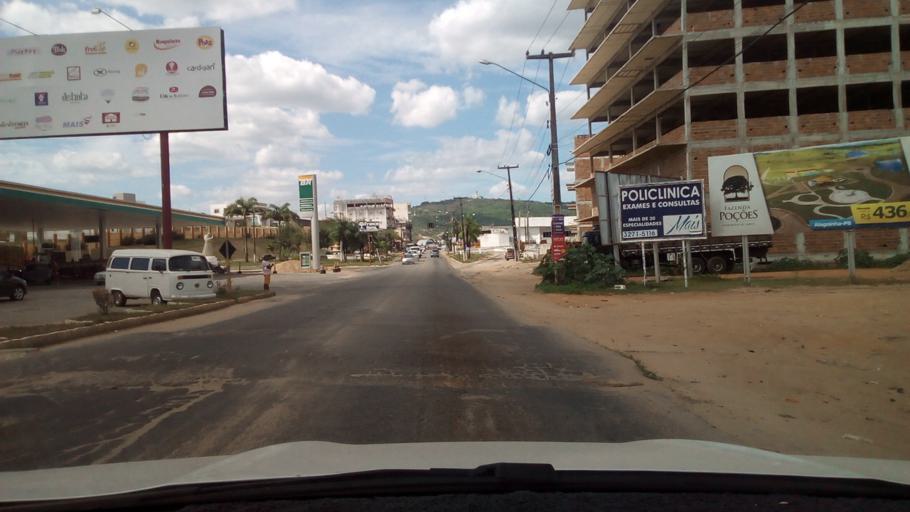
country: BR
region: Paraiba
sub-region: Guarabira
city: Guarabira
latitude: -6.8592
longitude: -35.4962
